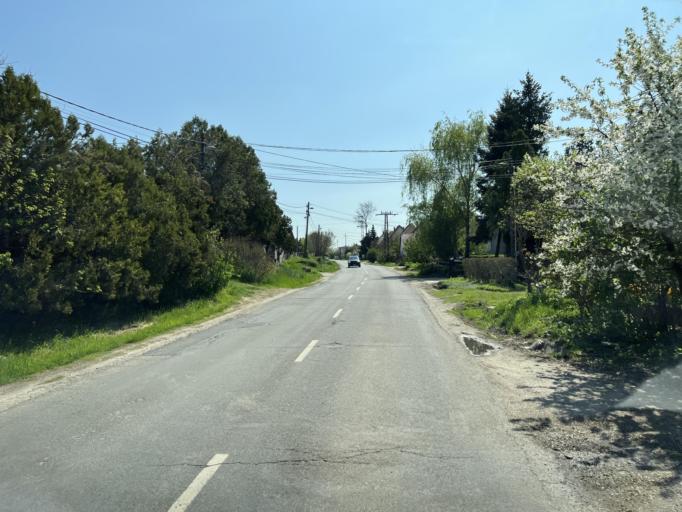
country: HU
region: Pest
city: Ocsa
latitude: 47.2983
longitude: 19.2156
